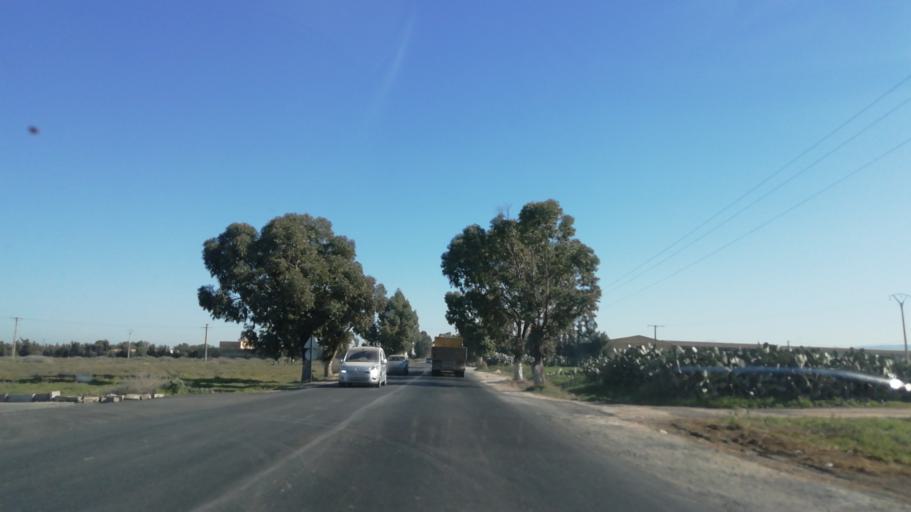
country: DZ
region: Relizane
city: Zemoura
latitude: 35.7561
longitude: 0.6747
